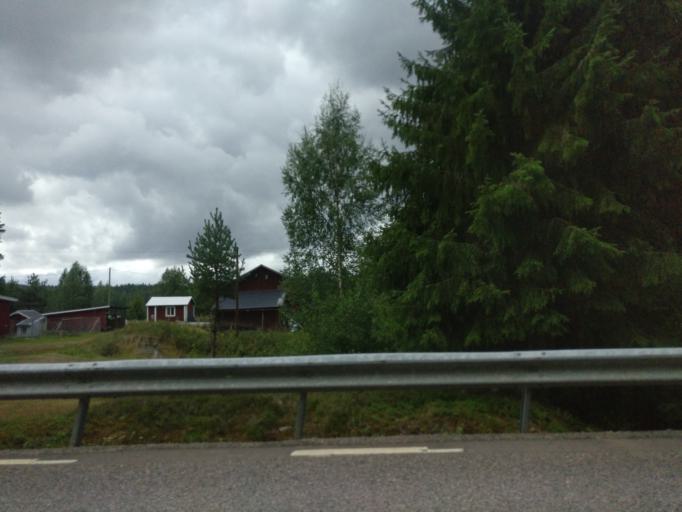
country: SE
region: Vaermland
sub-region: Torsby Kommun
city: Torsby
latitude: 60.7643
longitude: 12.7611
